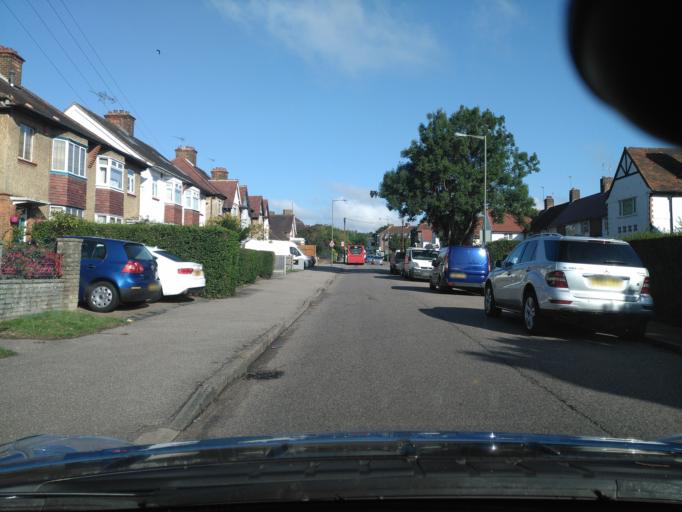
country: GB
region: England
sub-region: Greater London
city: High Barnet
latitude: 51.6456
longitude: -0.2138
